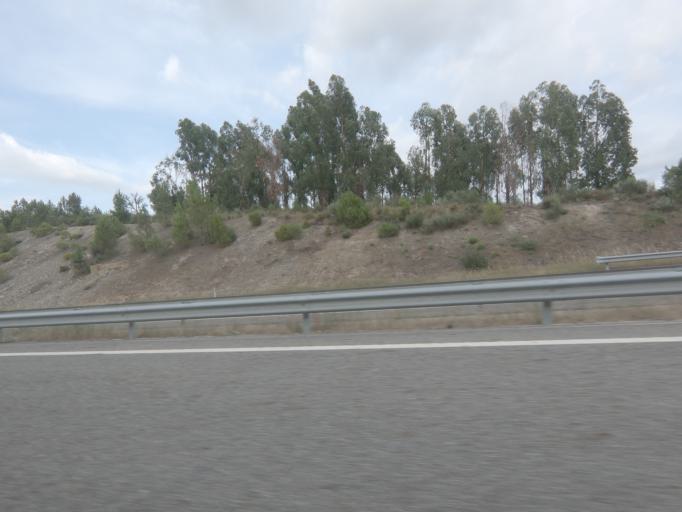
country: PT
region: Vila Real
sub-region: Chaves
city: Chaves
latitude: 41.6968
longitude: -7.5530
